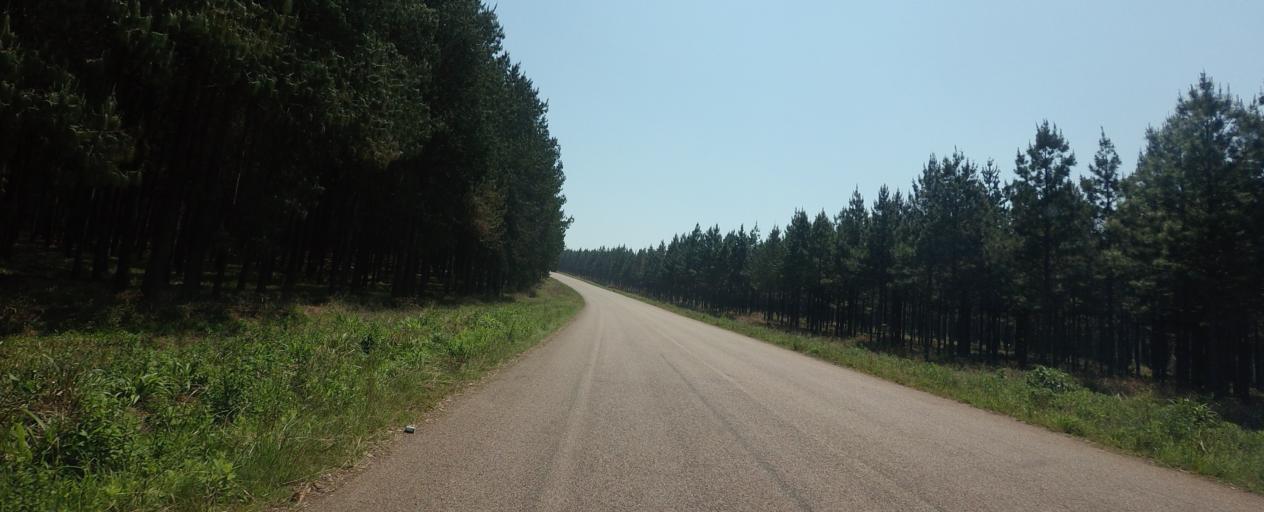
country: ZA
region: Mpumalanga
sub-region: Ehlanzeni District
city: Graksop
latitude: -25.0534
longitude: 30.8185
